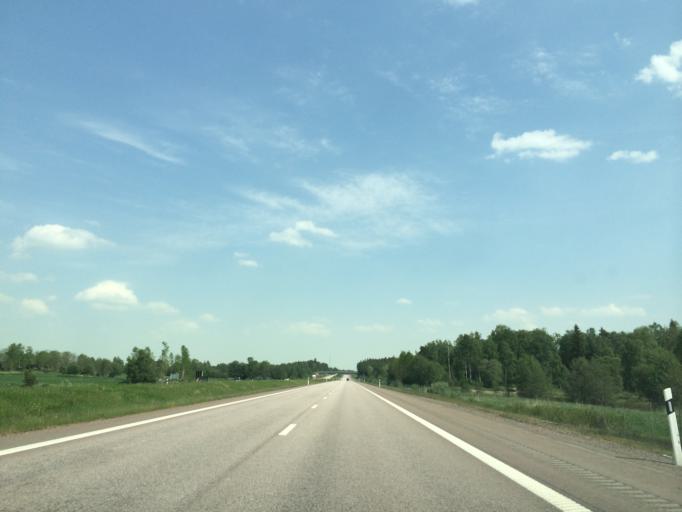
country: SE
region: OEstergoetland
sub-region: Odeshogs Kommun
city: OEdeshoeg
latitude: 58.2398
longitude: 14.7279
